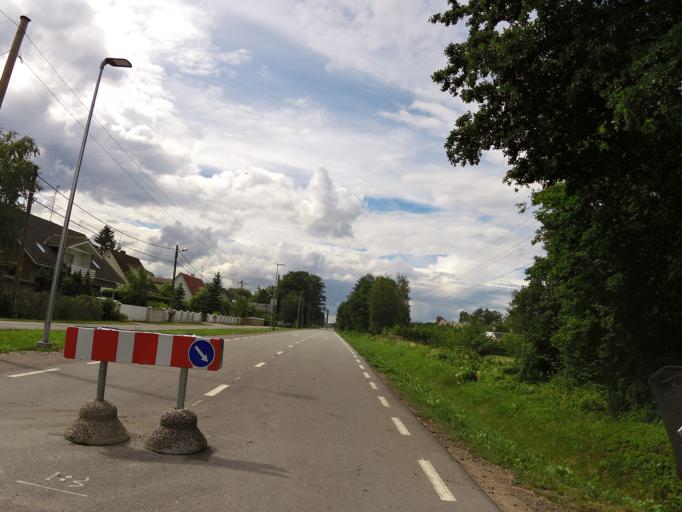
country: EE
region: Harju
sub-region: Tallinna linn
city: Tallinn
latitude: 59.4261
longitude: 24.6816
